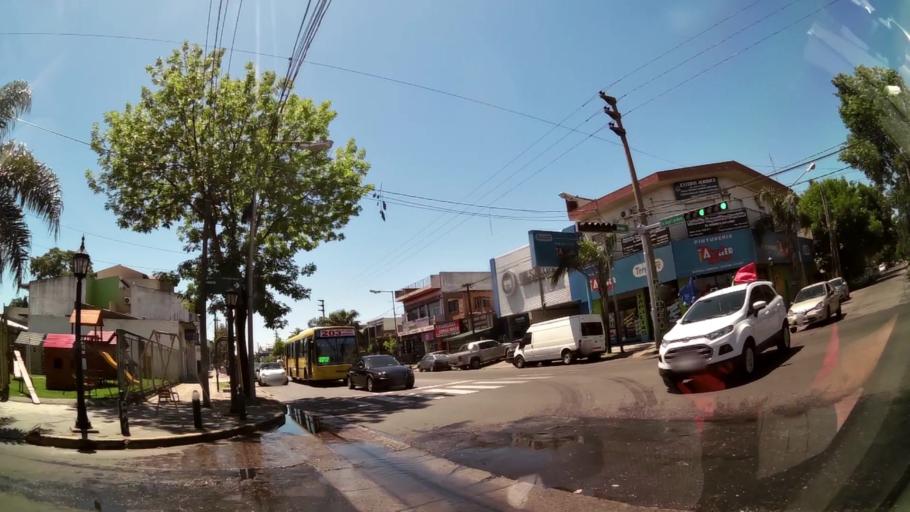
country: AR
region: Buenos Aires
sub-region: Partido de Tigre
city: Tigre
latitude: -34.4943
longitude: -58.6318
